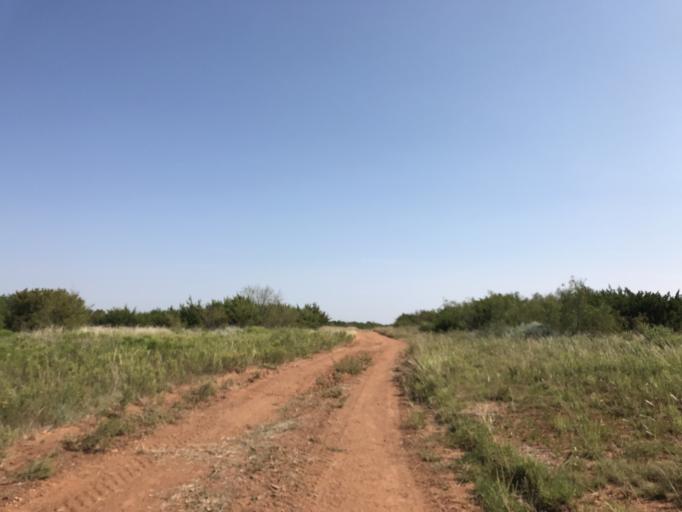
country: US
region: Oklahoma
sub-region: Beckham County
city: Erick
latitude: 35.0482
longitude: -99.8313
